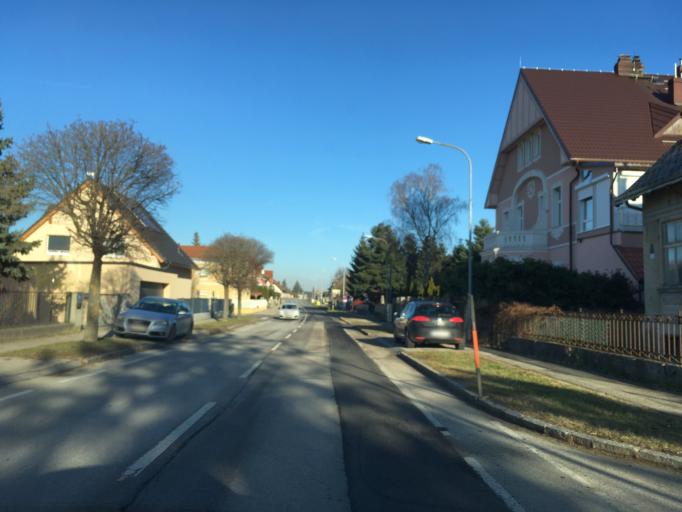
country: AT
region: Lower Austria
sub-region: Politischer Bezirk Tulln
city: Wordern
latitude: 48.3285
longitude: 16.2186
